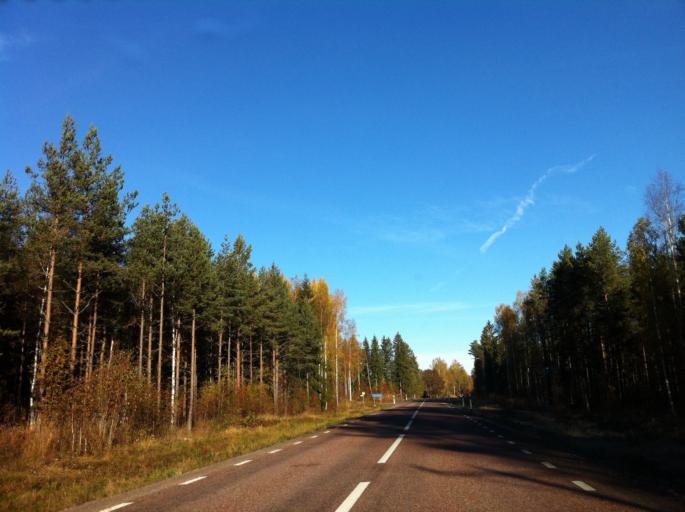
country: SE
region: Gaevleborg
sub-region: Gavle Kommun
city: Gavle
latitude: 60.5702
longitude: 17.1293
